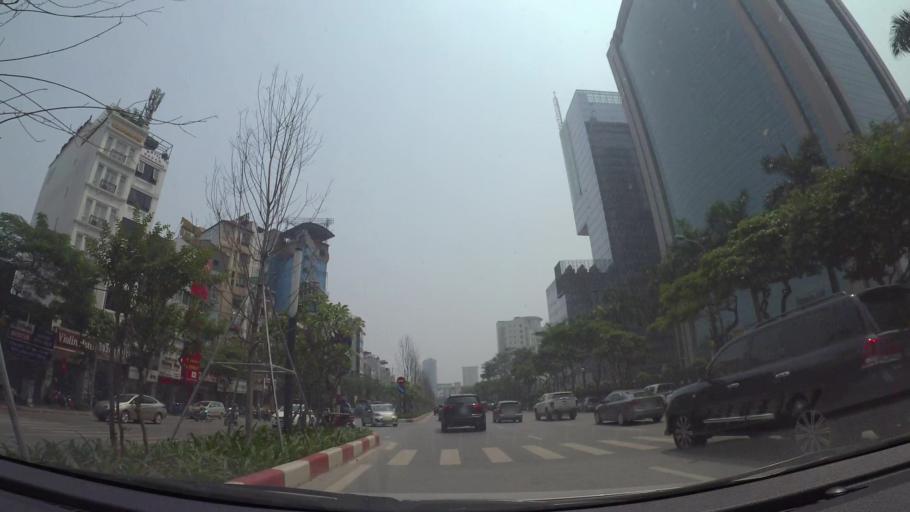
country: VN
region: Ha Noi
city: Thanh Xuan
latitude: 21.0079
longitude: 105.7968
